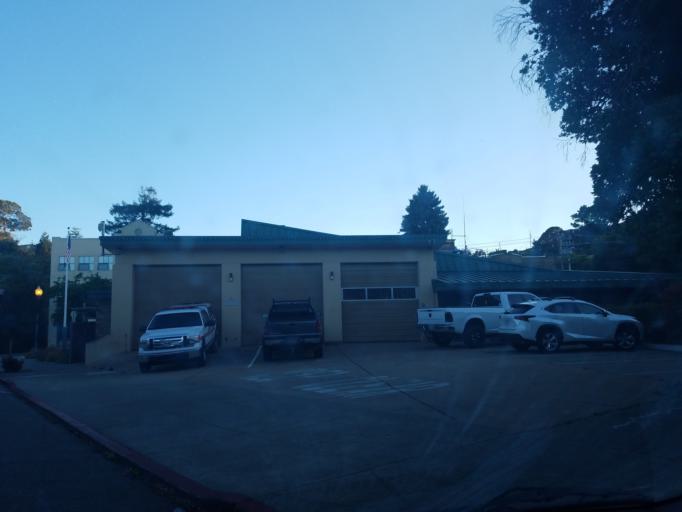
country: US
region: California
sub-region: Contra Costa County
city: North Richmond
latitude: 37.9263
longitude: -122.3852
